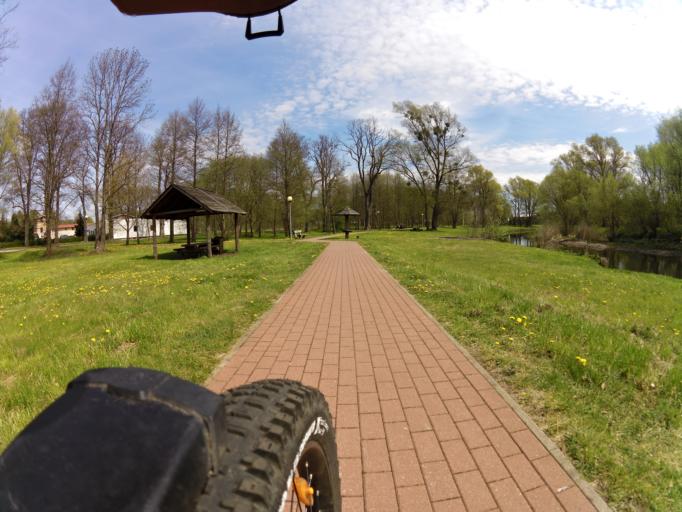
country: PL
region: West Pomeranian Voivodeship
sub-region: Powiat lobeski
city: Resko
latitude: 53.7734
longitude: 15.3966
